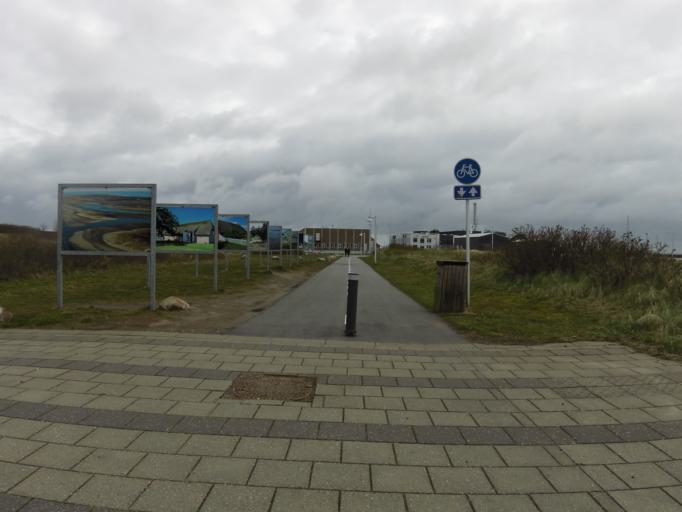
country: DE
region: Schleswig-Holstein
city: List
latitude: 55.0865
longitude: 8.5628
